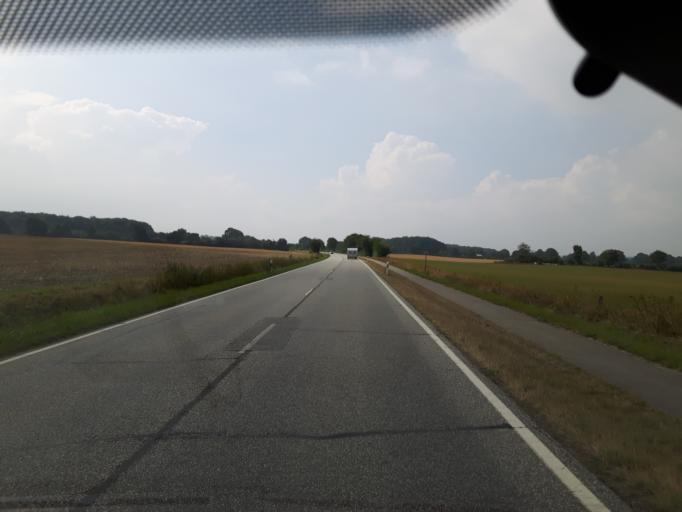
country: DE
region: Schleswig-Holstein
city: Goosefeld
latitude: 54.4238
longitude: 9.8044
